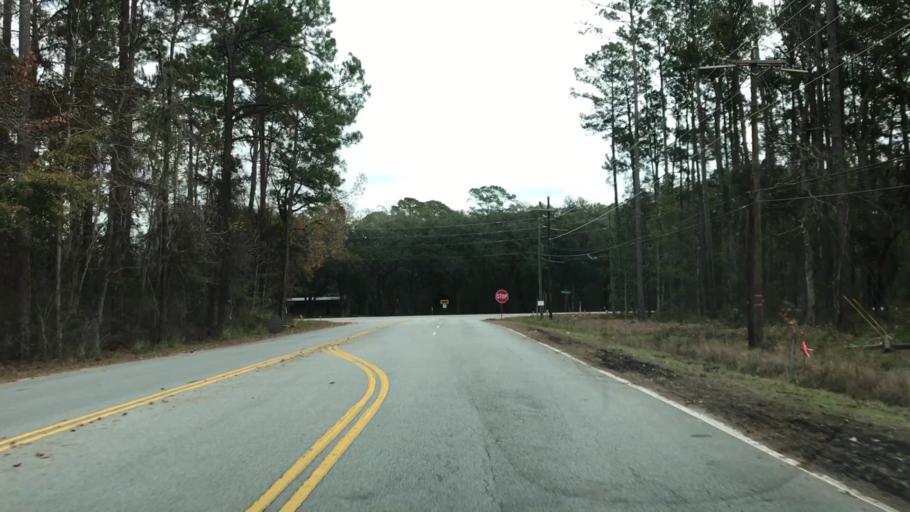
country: US
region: South Carolina
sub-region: Beaufort County
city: Burton
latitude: 32.4187
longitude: -80.7317
